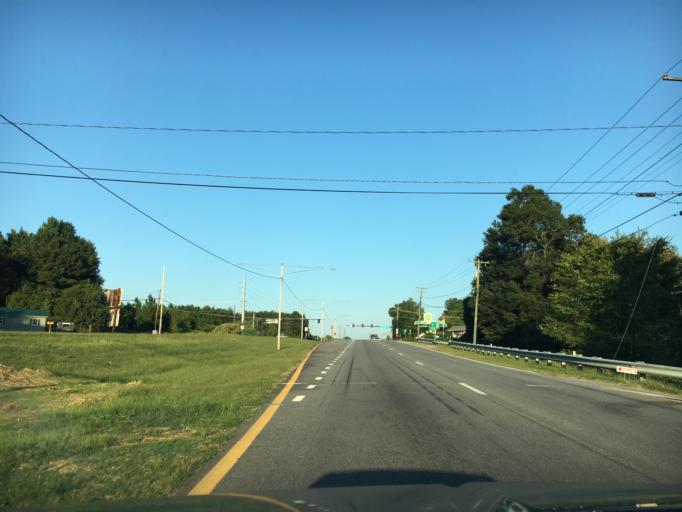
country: US
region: Virginia
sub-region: City of Danville
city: Danville
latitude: 36.5809
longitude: -79.3239
